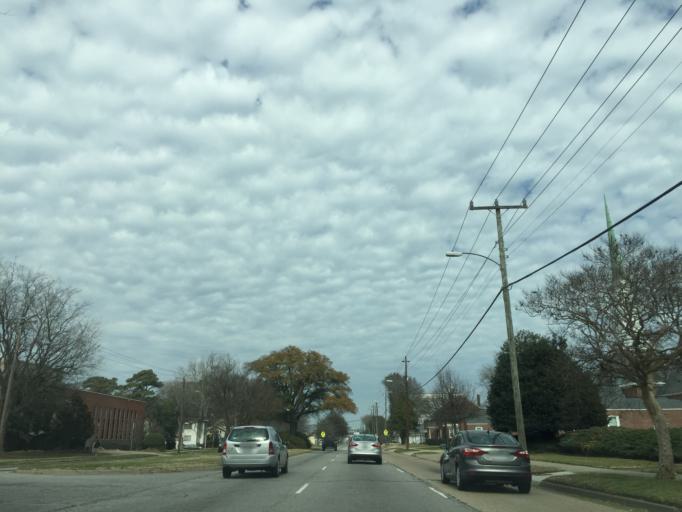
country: US
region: Virginia
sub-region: City of Norfolk
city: Norfolk
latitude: 36.9086
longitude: -76.2752
